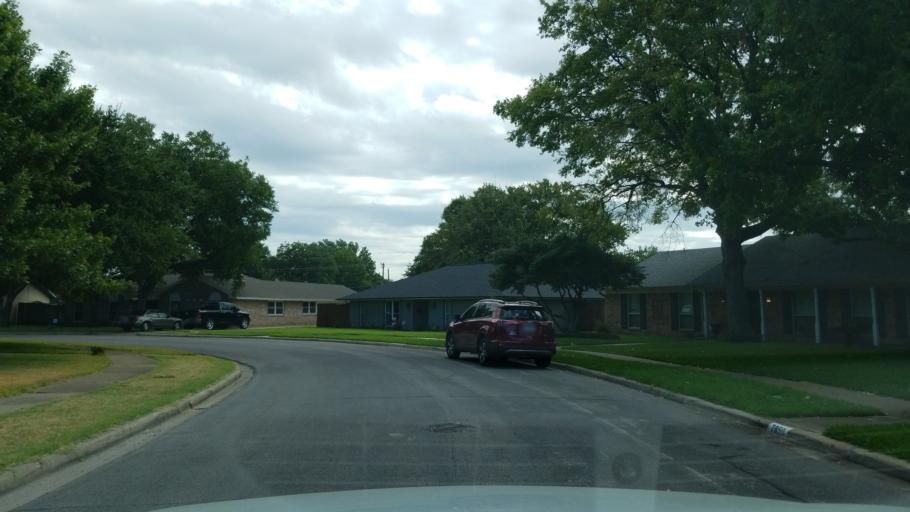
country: US
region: Texas
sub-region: Dallas County
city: Richardson
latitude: 32.9669
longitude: -96.7700
